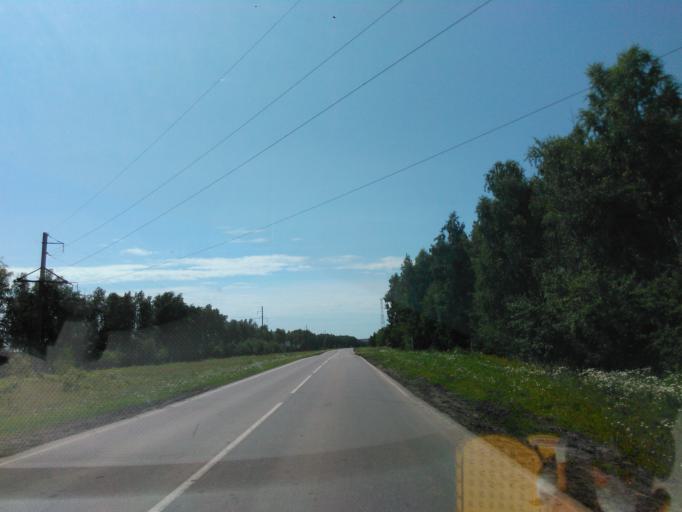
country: RU
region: Penza
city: Belinskiy
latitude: 52.9682
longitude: 43.4667
